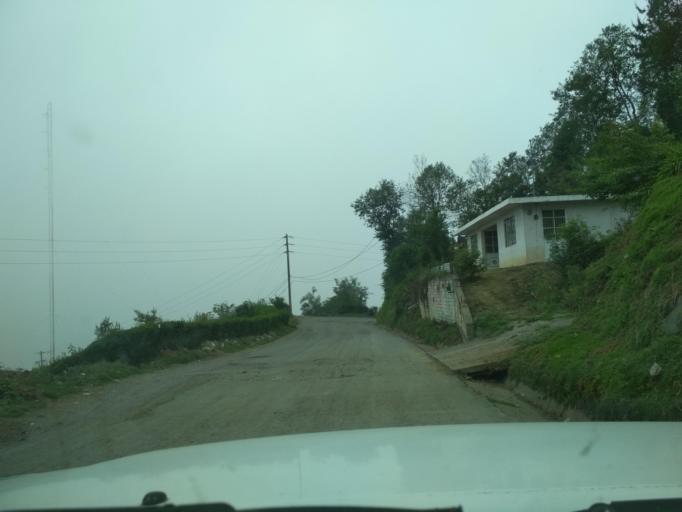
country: MX
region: Veracruz
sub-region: La Perla
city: Chilapa
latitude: 18.9724
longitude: -97.1711
